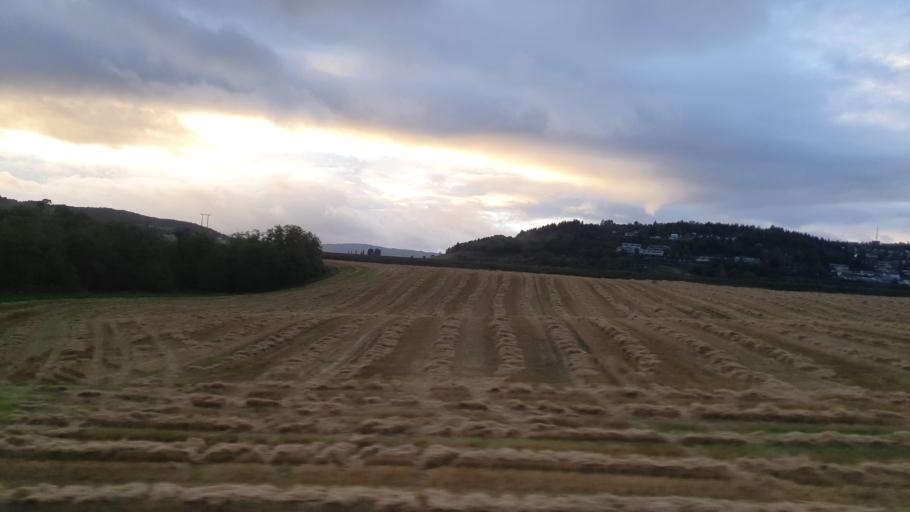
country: NO
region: Nord-Trondelag
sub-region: Levanger
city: Skogn
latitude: 63.6904
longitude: 11.1872
